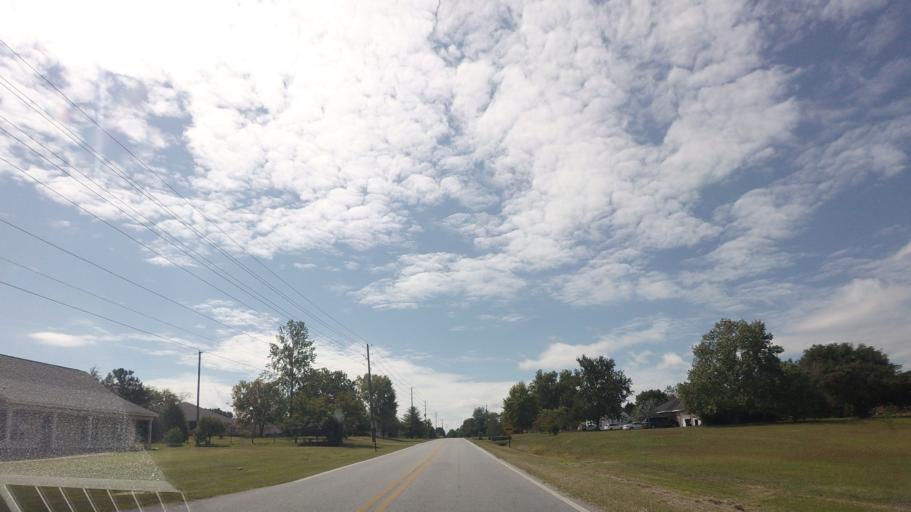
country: US
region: Georgia
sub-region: Houston County
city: Centerville
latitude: 32.5992
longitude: -83.7093
